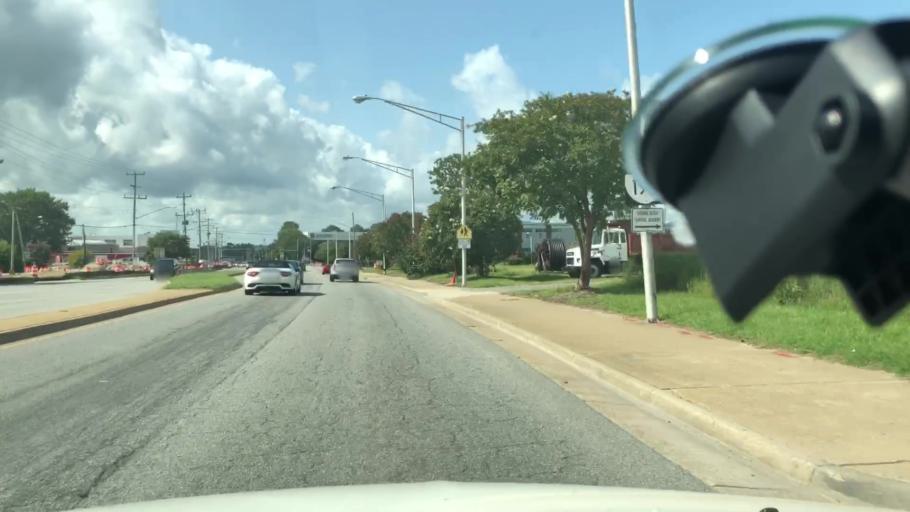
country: US
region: Virginia
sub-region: City of Chesapeake
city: Chesapeake
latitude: 36.8450
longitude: -76.1570
